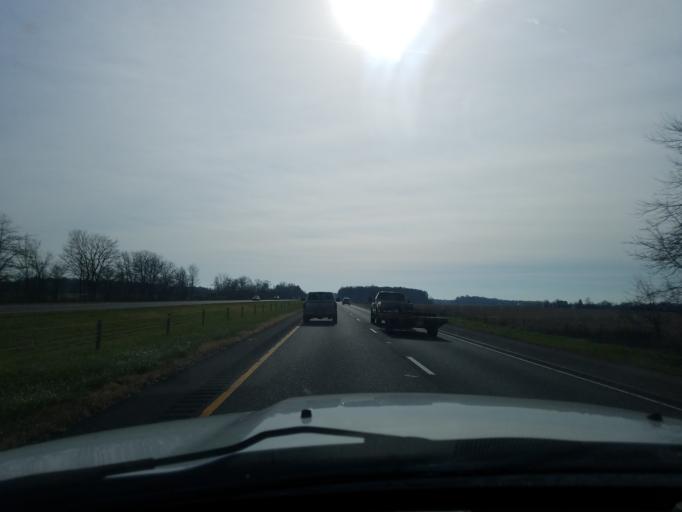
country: US
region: Indiana
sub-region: Delaware County
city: Daleville
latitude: 40.1556
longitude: -85.5670
